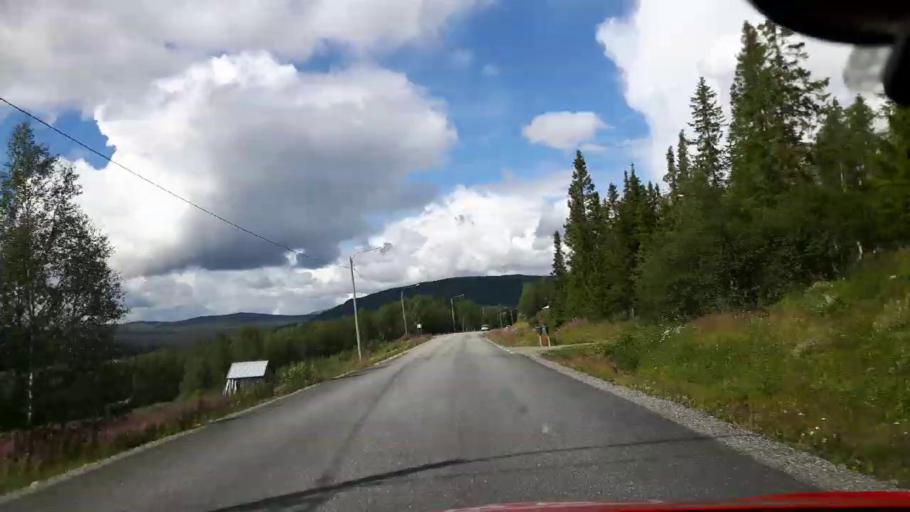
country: NO
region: Nordland
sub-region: Hattfjelldal
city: Hattfjelldal
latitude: 65.0627
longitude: 14.8672
